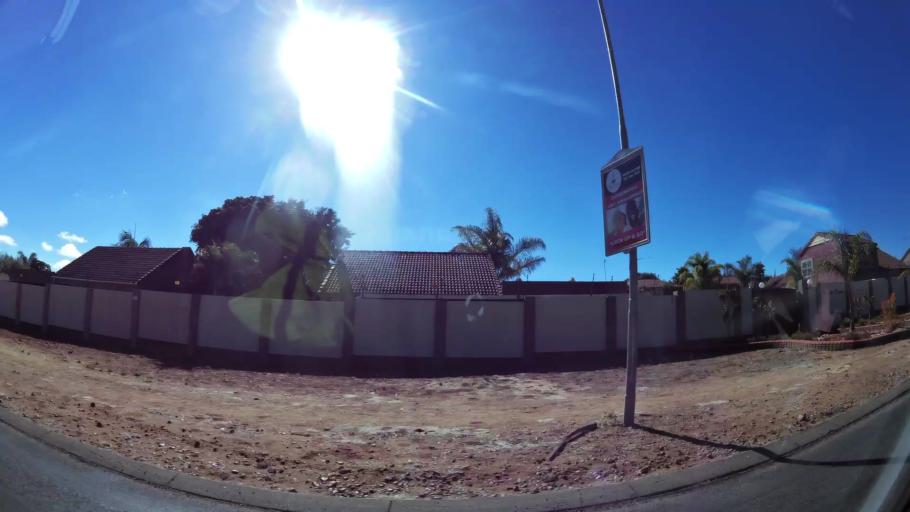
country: ZA
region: Limpopo
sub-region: Capricorn District Municipality
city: Polokwane
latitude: -23.9006
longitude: 29.4716
